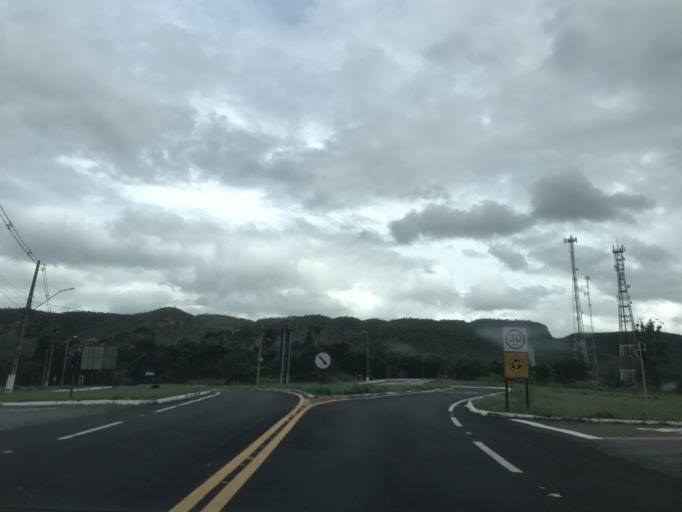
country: BR
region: Goias
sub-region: Caldas Novas
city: Caldas Novas
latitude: -17.7661
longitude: -48.7574
